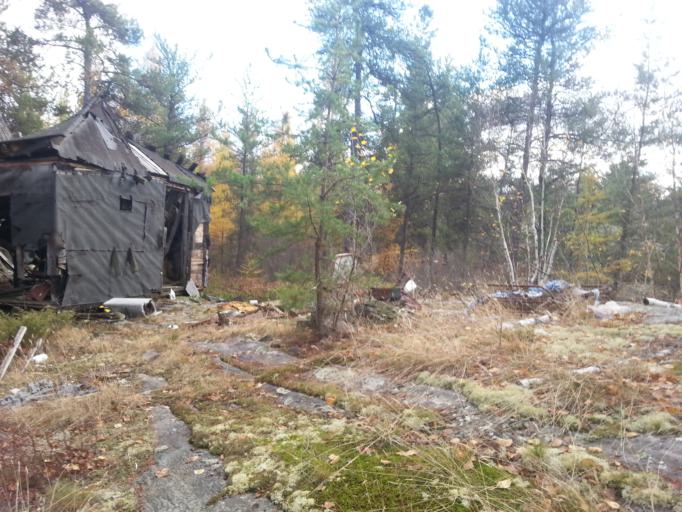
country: CA
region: Ontario
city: Greater Sudbury
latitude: 46.1192
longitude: -80.6578
